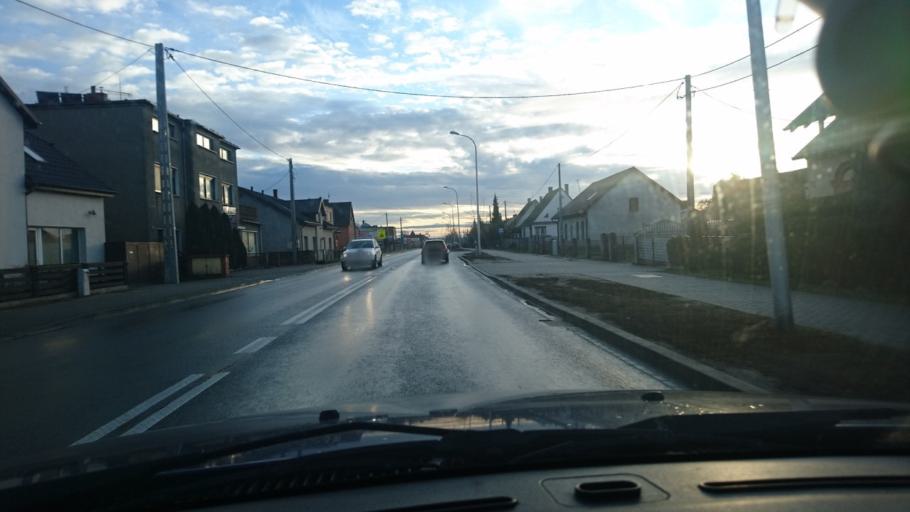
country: PL
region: Greater Poland Voivodeship
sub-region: Powiat kepinski
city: Kepno
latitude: 51.2968
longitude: 17.9971
